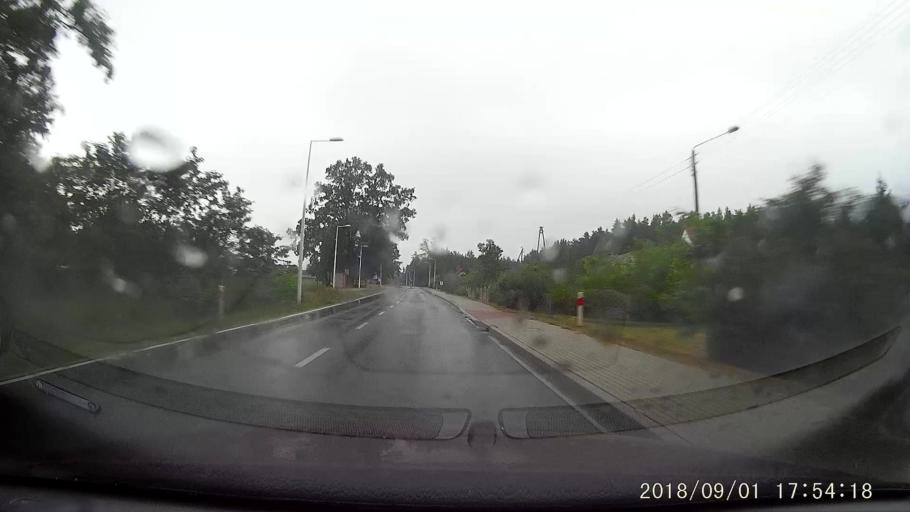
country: PL
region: Lubusz
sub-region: Powiat zaganski
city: Ilowa
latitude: 51.4701
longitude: 15.1994
